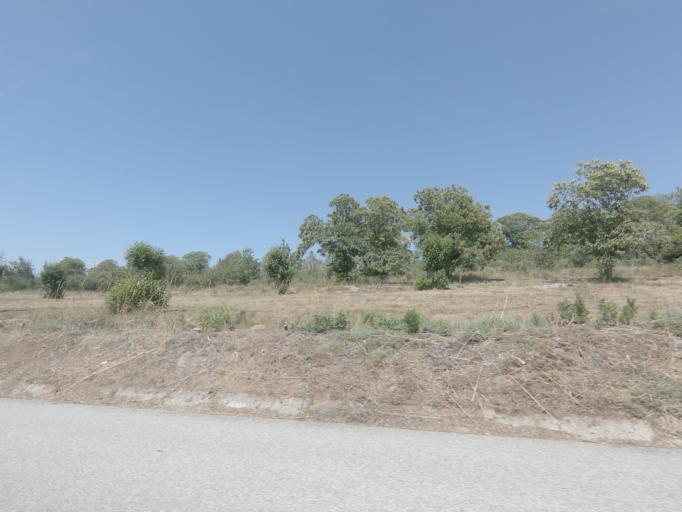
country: PT
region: Viseu
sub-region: Tarouca
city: Tarouca
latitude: 40.9895
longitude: -7.8097
